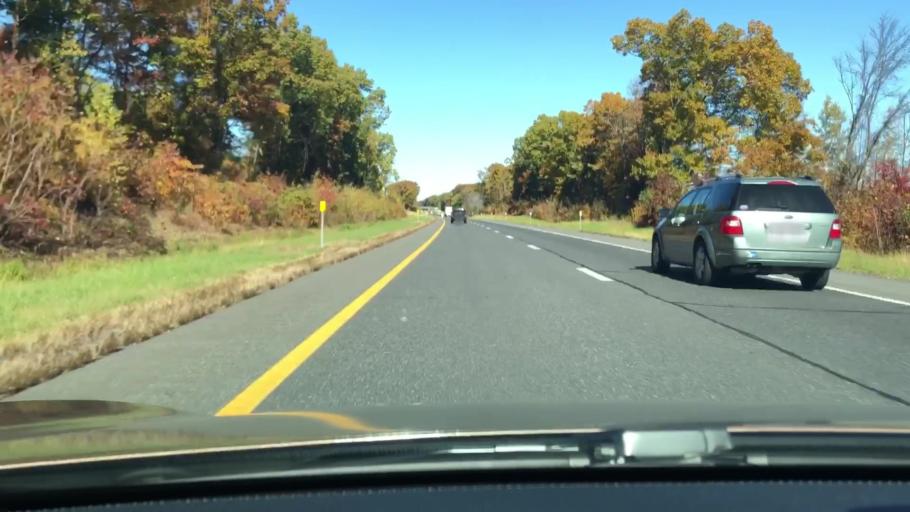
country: US
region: New York
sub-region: Ulster County
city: New Paltz
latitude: 41.7599
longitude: -74.0562
